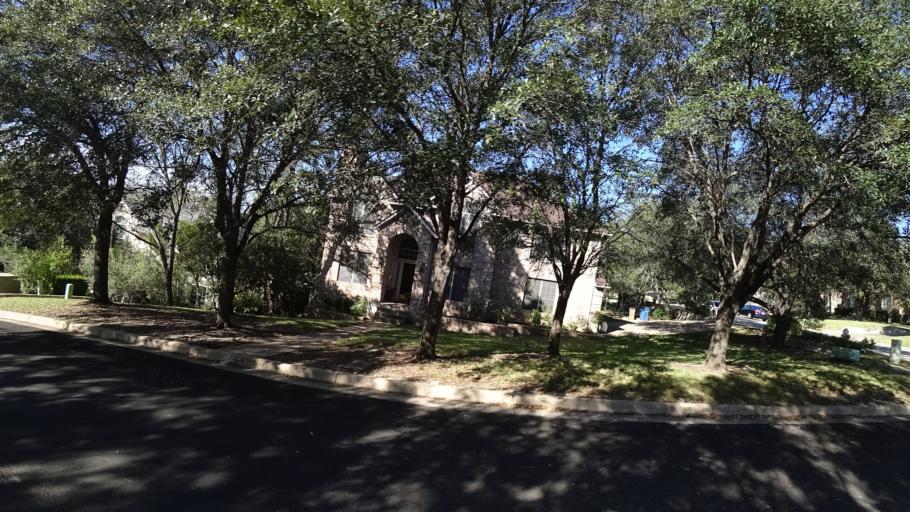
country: US
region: Texas
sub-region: Williamson County
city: Jollyville
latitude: 30.4135
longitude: -97.7718
